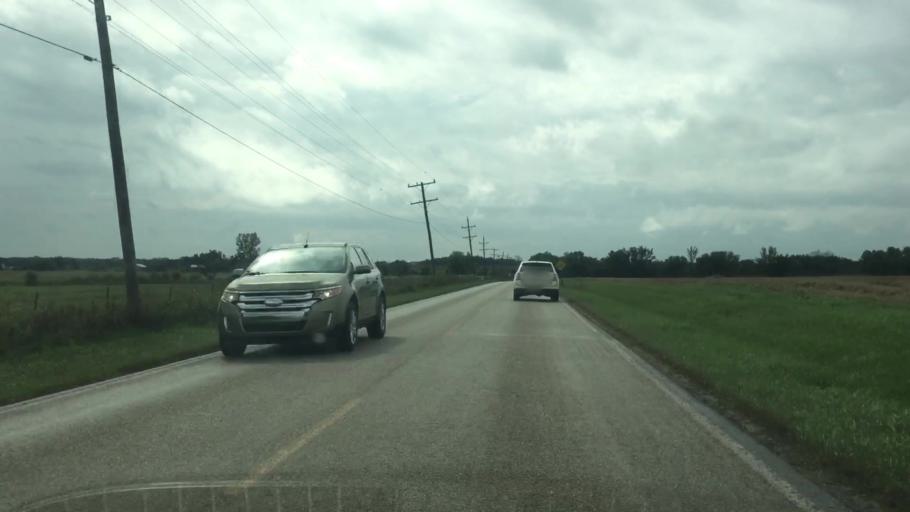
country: US
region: Kansas
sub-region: Allen County
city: Humboldt
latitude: 37.8558
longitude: -95.4369
